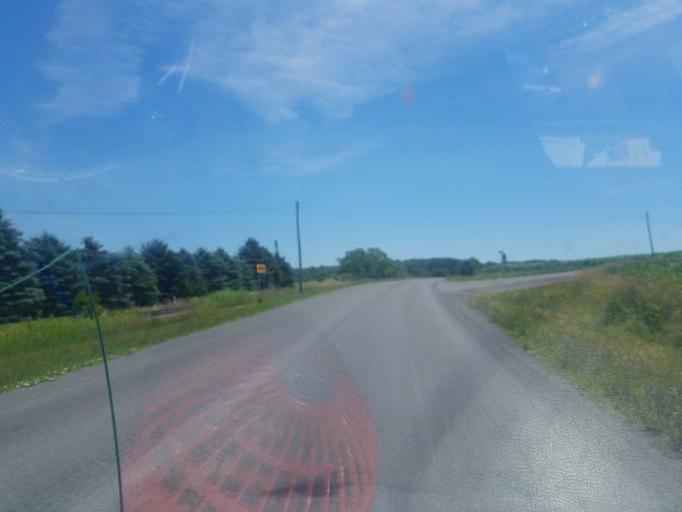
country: US
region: New York
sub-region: Yates County
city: Penn Yan
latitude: 42.6515
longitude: -77.0183
